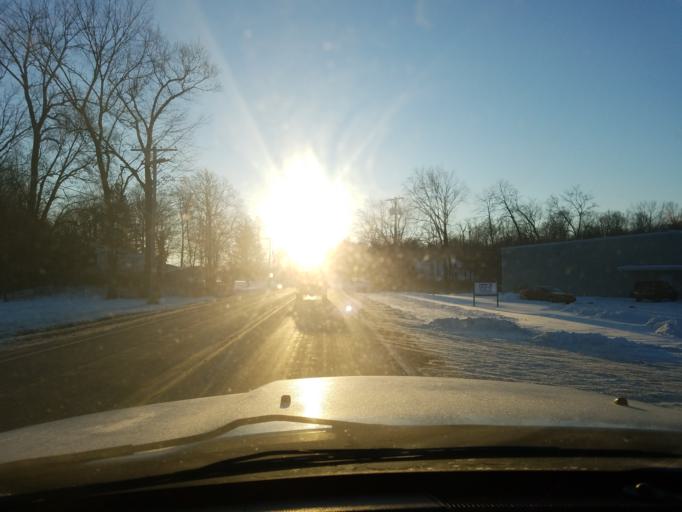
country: US
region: Indiana
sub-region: Marshall County
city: Bremen
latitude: 41.4488
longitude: -86.0888
